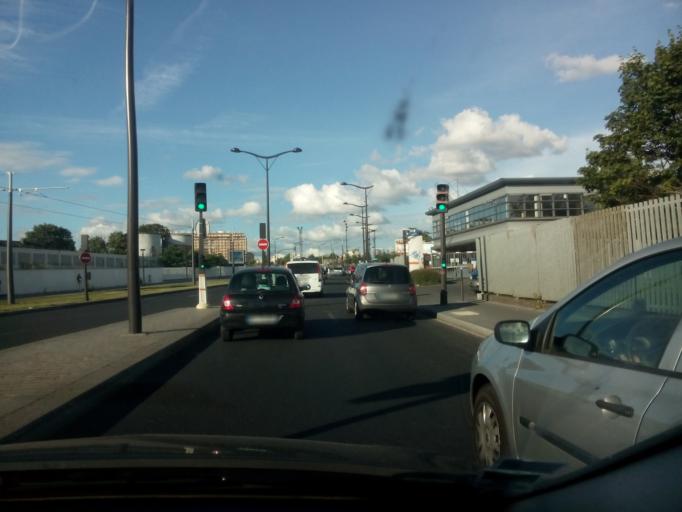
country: FR
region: Ile-de-France
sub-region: Departement du Val-de-Marne
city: Ivry-sur-Seine
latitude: 48.8296
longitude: 2.3910
